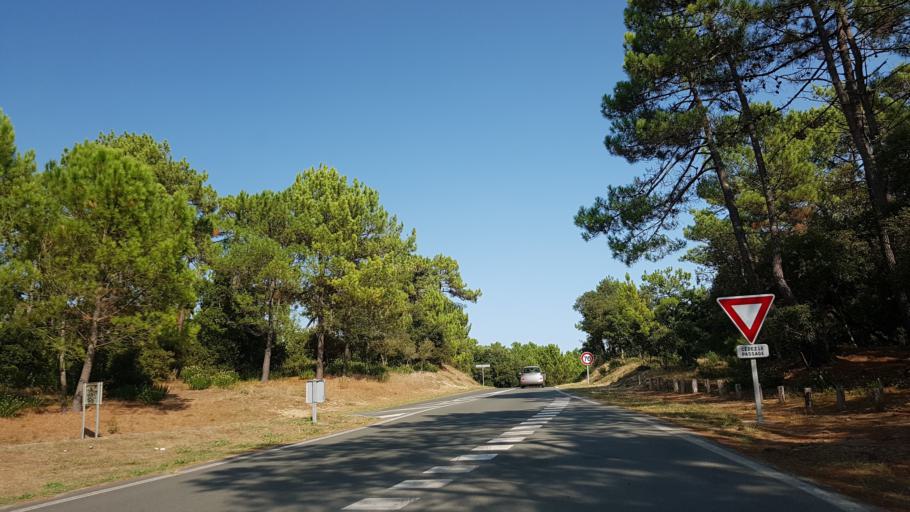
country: FR
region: Poitou-Charentes
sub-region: Departement de la Charente-Maritime
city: Les Mathes
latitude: 45.6992
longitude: -1.2280
